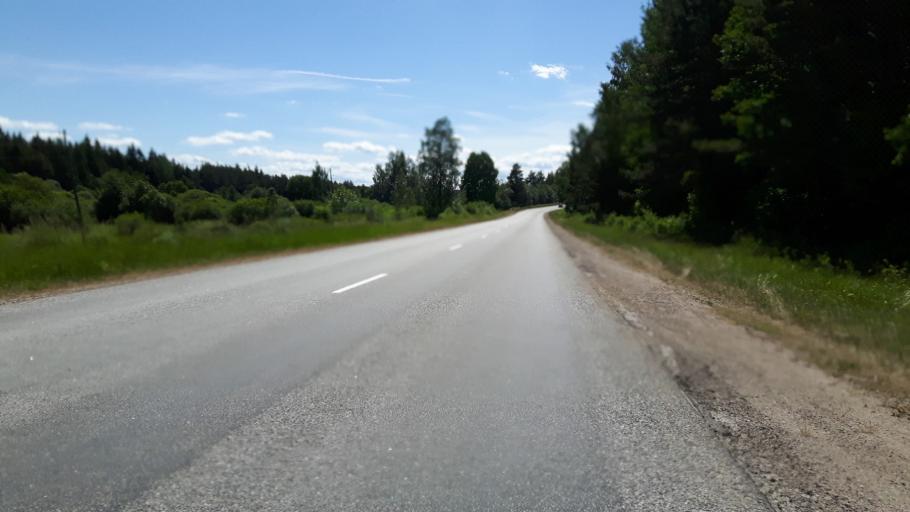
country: LV
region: Kandava
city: Kandava
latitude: 57.0275
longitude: 22.7757
